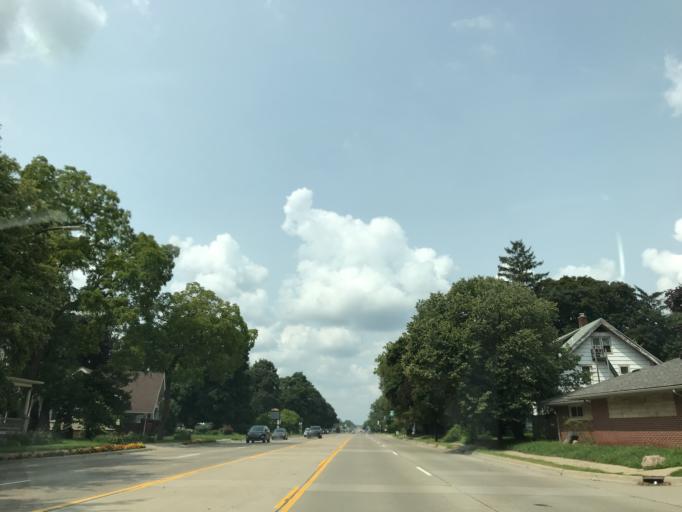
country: US
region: Michigan
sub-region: Washtenaw County
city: Ypsilanti
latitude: 42.2465
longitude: -83.6303
